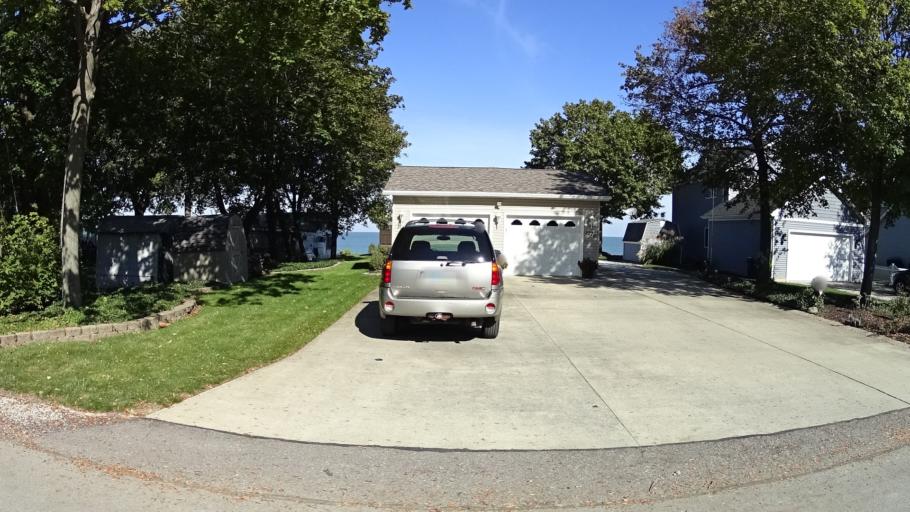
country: US
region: Ohio
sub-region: Lorain County
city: Vermilion-on-the-Lake
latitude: 41.4291
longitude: -82.3113
